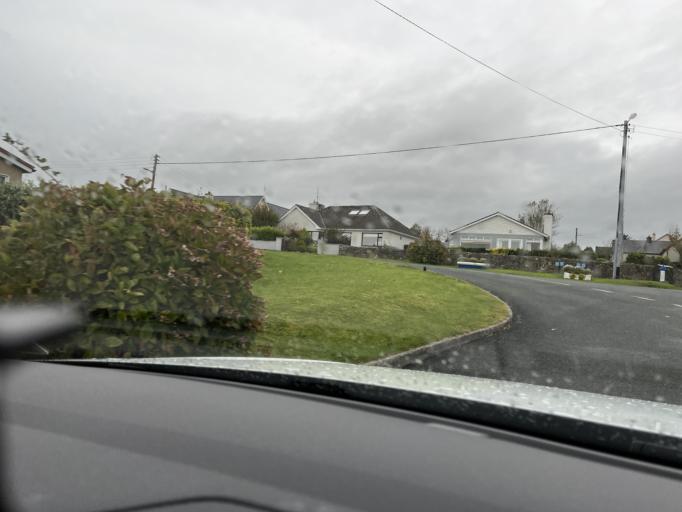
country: IE
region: Connaught
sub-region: Sligo
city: Strandhill
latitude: 54.3079
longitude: -8.5524
